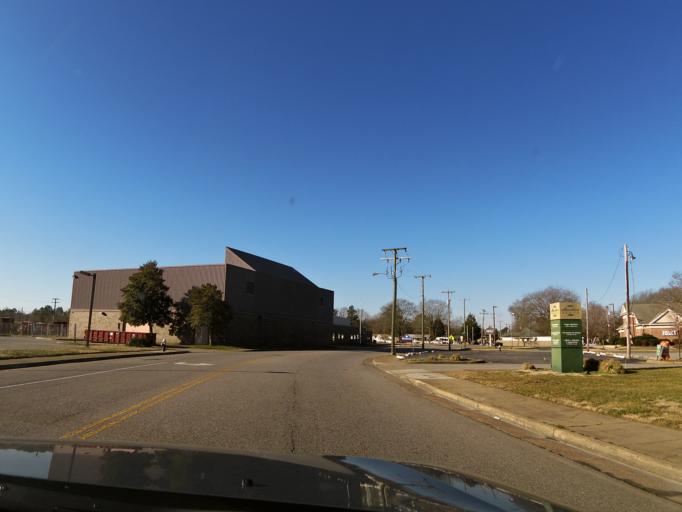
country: US
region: Virginia
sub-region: City of Hopewell
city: Hopewell
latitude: 37.3018
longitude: -77.2875
